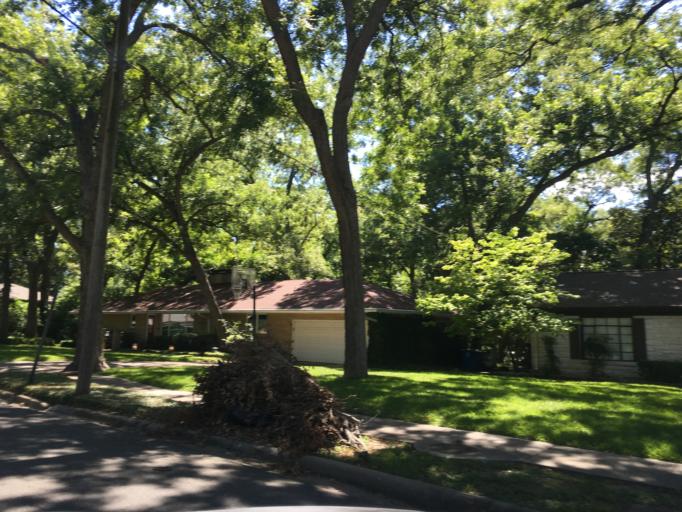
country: US
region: Texas
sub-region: Dallas County
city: Highland Park
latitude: 32.8385
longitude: -96.7041
